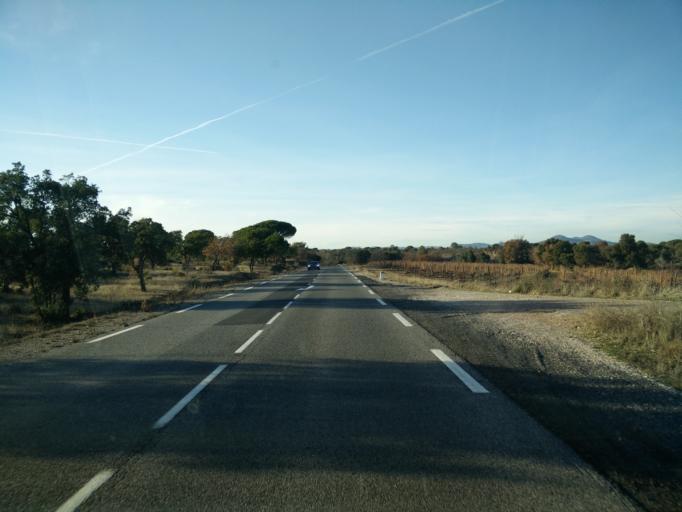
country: FR
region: Provence-Alpes-Cote d'Azur
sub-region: Departement du Var
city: La Garde-Freinet
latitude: 43.3534
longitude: 6.4164
